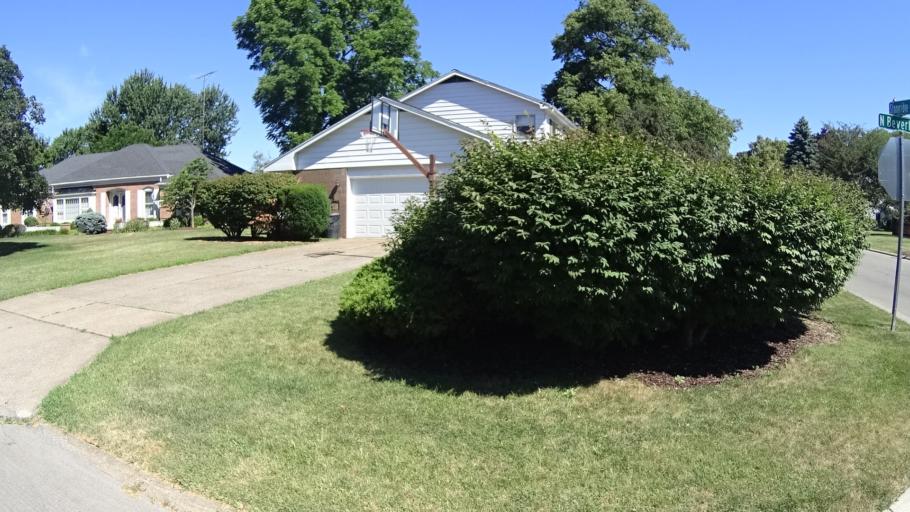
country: US
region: Ohio
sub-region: Erie County
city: Sandusky
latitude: 41.4195
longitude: -82.6962
